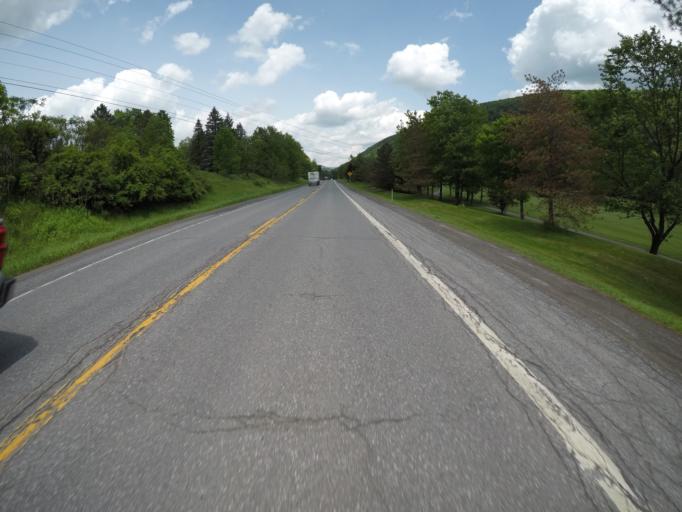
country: US
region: New York
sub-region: Delaware County
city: Stamford
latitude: 42.1668
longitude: -74.6156
